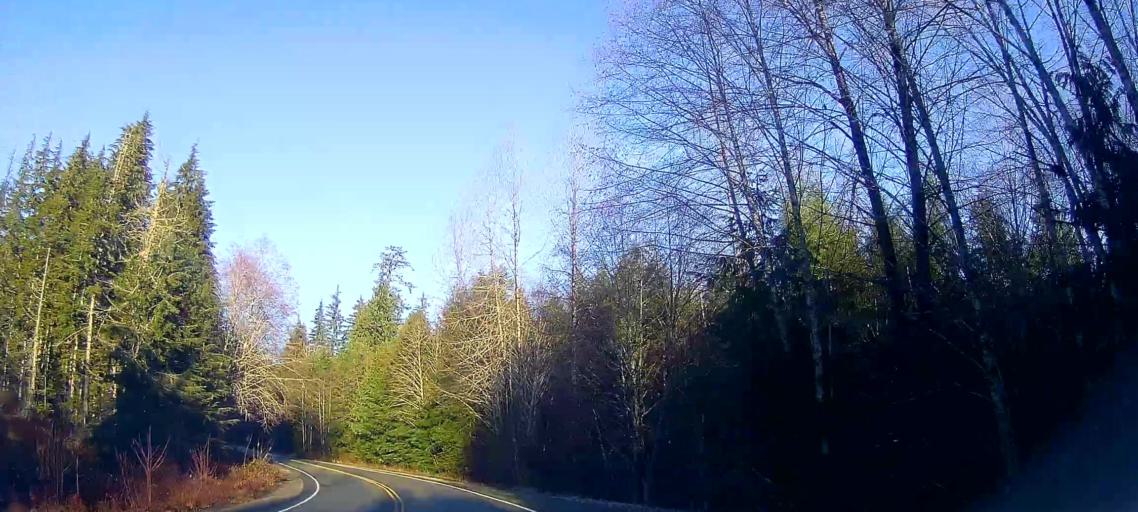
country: US
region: Washington
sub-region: Snohomish County
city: Darrington
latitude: 48.6426
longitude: -121.7300
